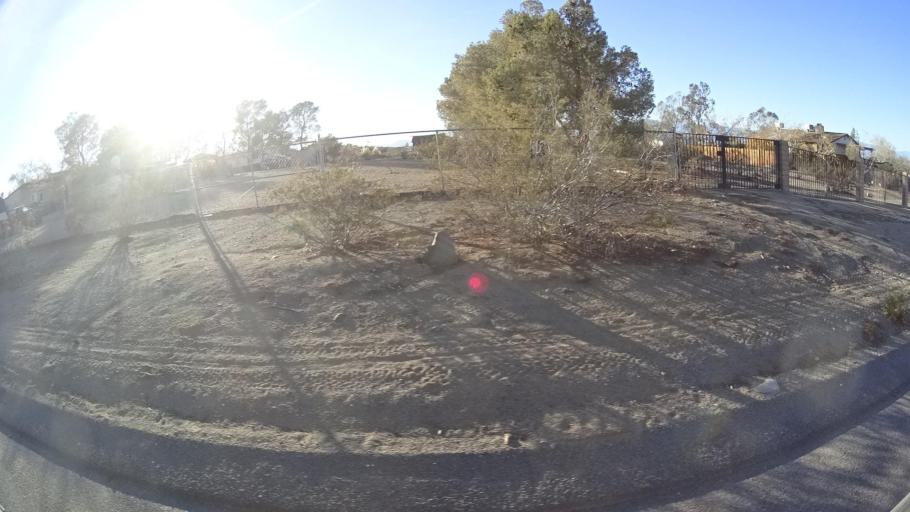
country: US
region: California
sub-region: Kern County
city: Ridgecrest
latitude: 35.5870
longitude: -117.6615
